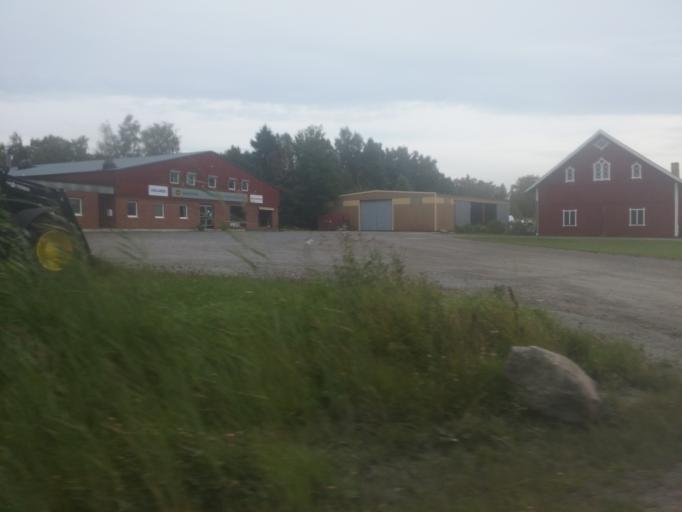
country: SE
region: OEstergoetland
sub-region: Norrkopings Kommun
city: Krokek
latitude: 58.5781
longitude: 16.3947
